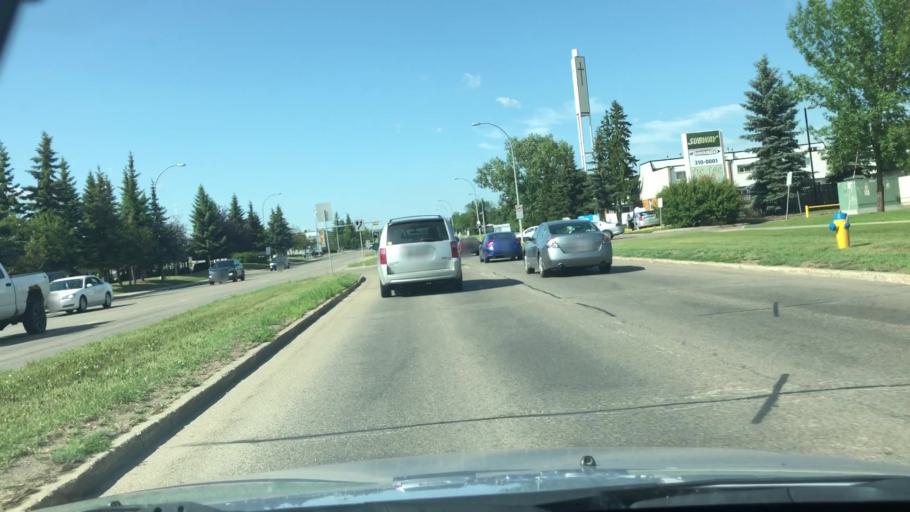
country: CA
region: Alberta
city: Edmonton
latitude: 53.6000
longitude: -113.4429
